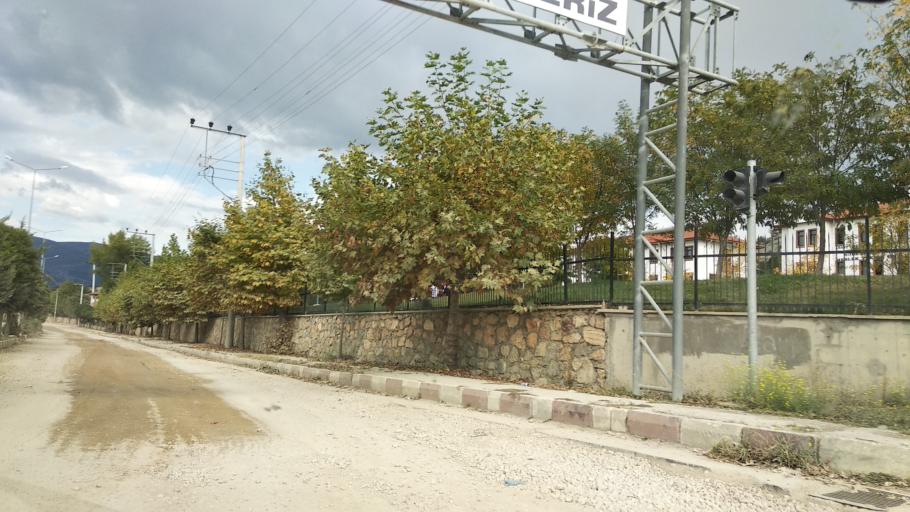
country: TR
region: Bolu
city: Mudurnu
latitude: 40.4783
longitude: 31.2104
